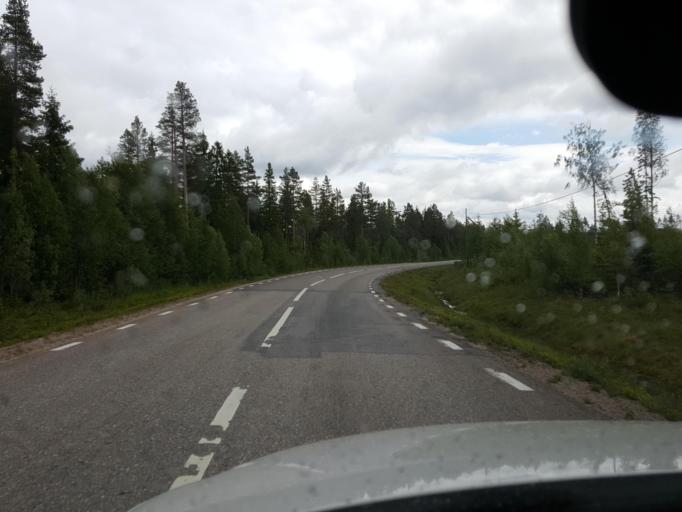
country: SE
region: Gaevleborg
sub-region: Ljusdals Kommun
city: Farila
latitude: 61.7601
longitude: 15.5147
